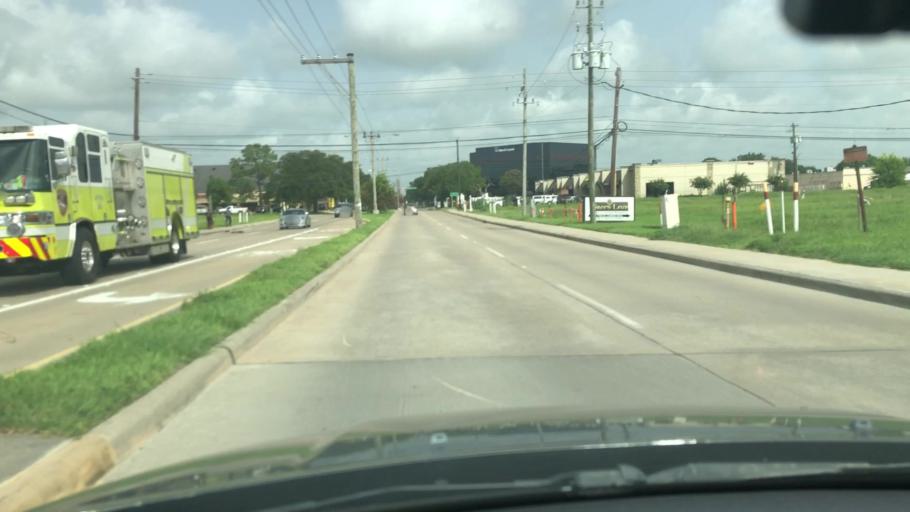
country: US
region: Texas
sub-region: Harris County
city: Webster
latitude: 29.5506
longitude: -95.1121
